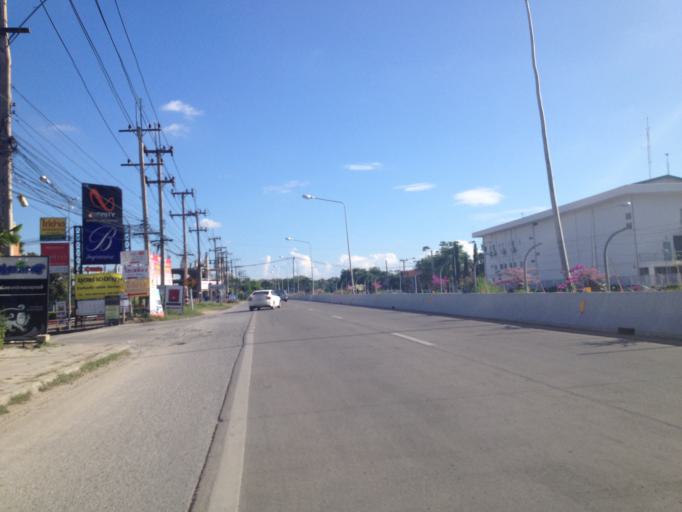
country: TH
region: Chiang Mai
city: Chiang Mai
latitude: 18.7982
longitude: 98.9613
